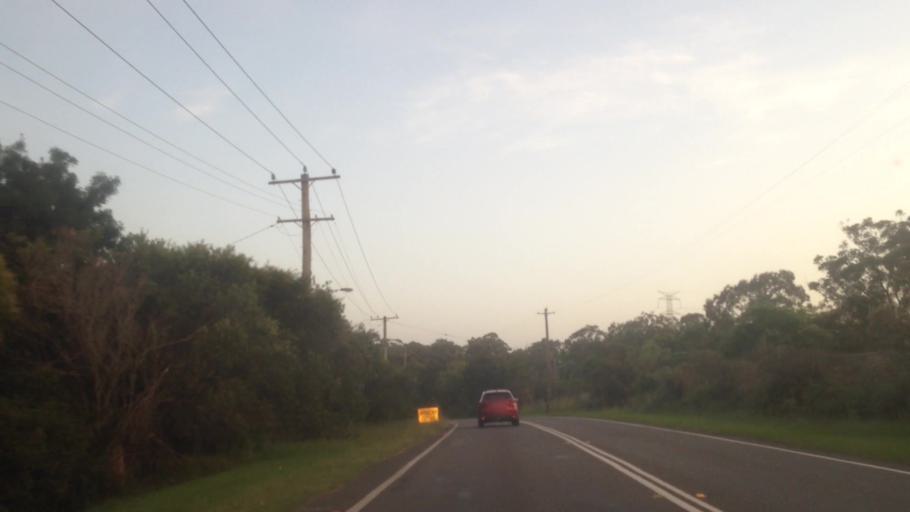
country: AU
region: New South Wales
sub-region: Lake Macquarie Shire
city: Dora Creek
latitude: -33.0961
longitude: 151.4974
